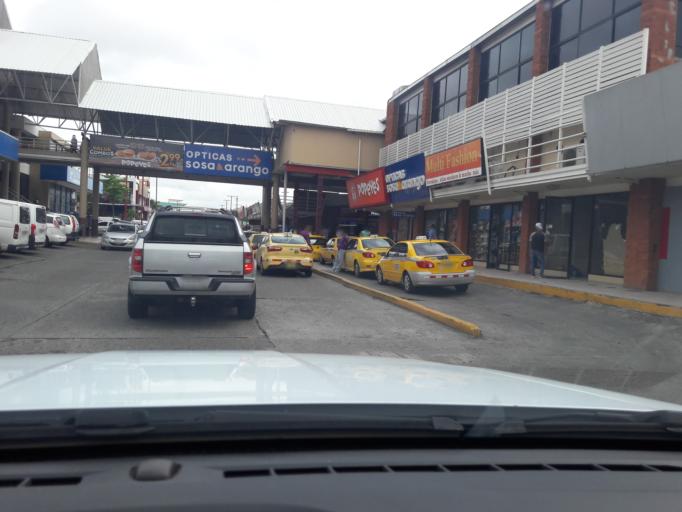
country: PA
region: Panama
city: San Miguelito
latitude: 9.0498
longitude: -79.5081
